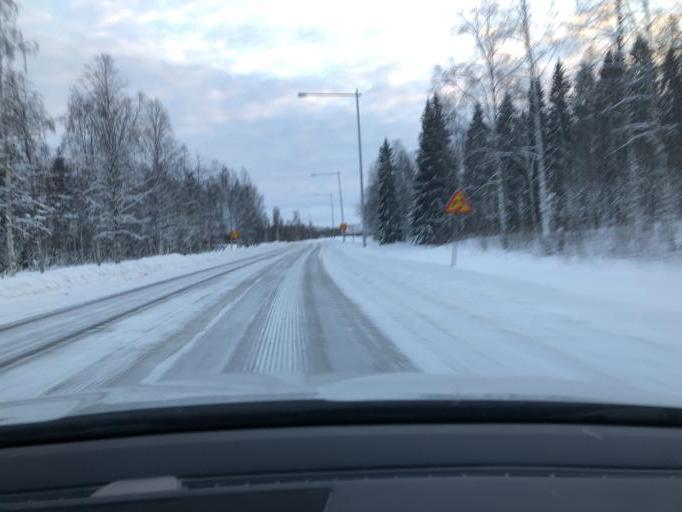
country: SE
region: Norrbotten
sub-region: Lulea Kommun
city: Lulea
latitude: 65.6203
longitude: 22.1284
